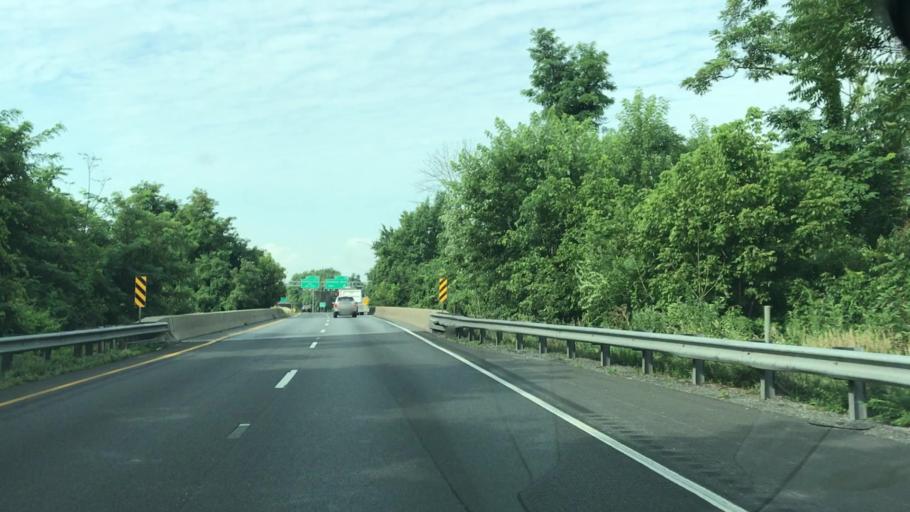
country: US
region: Maryland
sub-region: Washington County
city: Halfway
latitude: 39.6322
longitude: -77.7725
